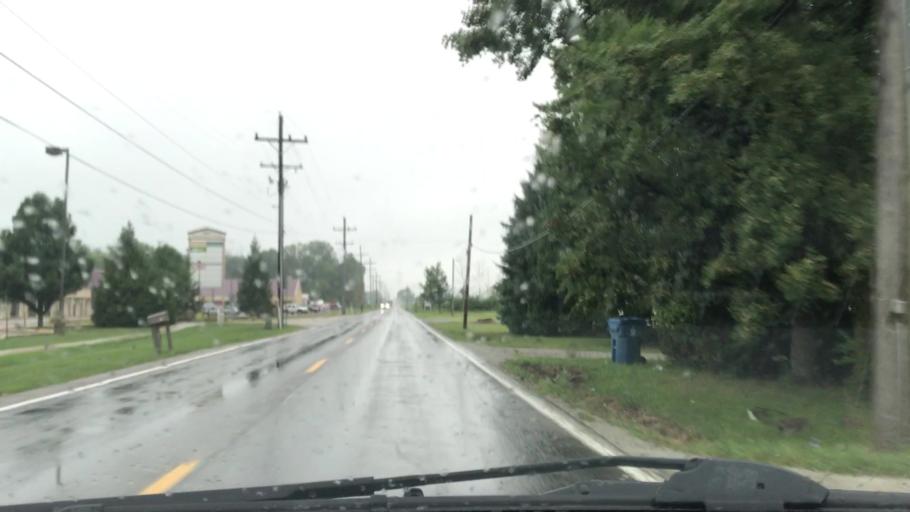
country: US
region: Indiana
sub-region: Hamilton County
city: Sheridan
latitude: 40.1298
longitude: -86.2292
